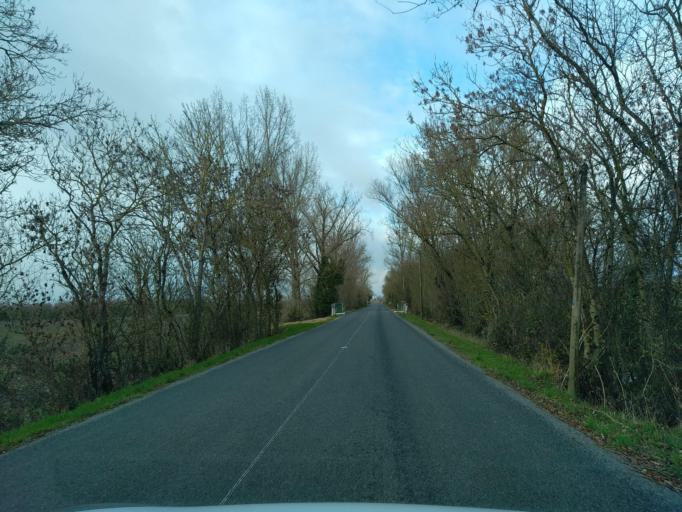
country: FR
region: Pays de la Loire
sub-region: Departement de la Vendee
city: Vix
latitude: 46.3417
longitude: -0.8277
